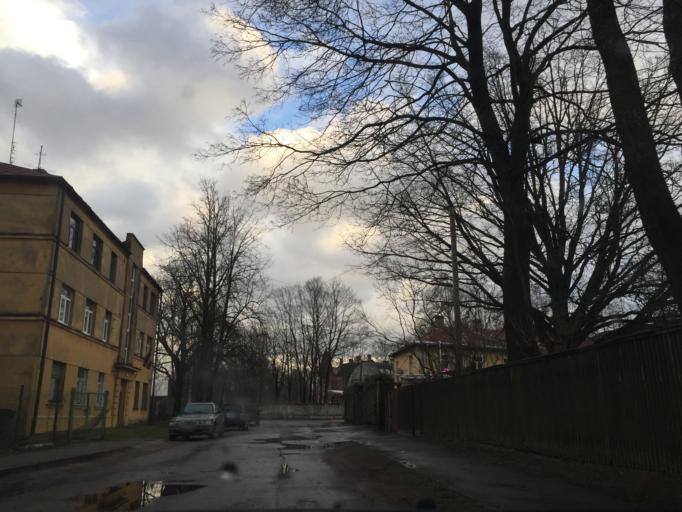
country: LV
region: Marupe
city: Marupe
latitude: 56.9378
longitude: 24.0517
